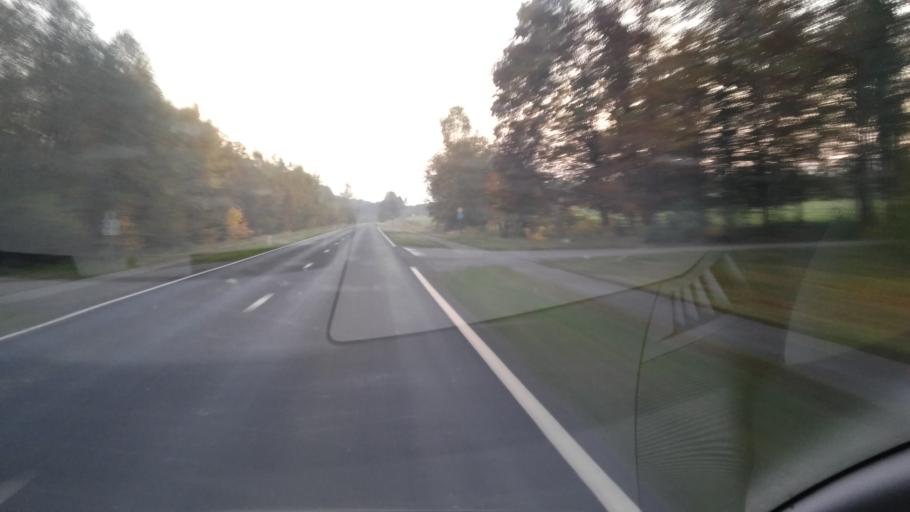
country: BE
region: Wallonia
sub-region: Province du Luxembourg
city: Etalle
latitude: 49.6477
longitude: 5.5778
